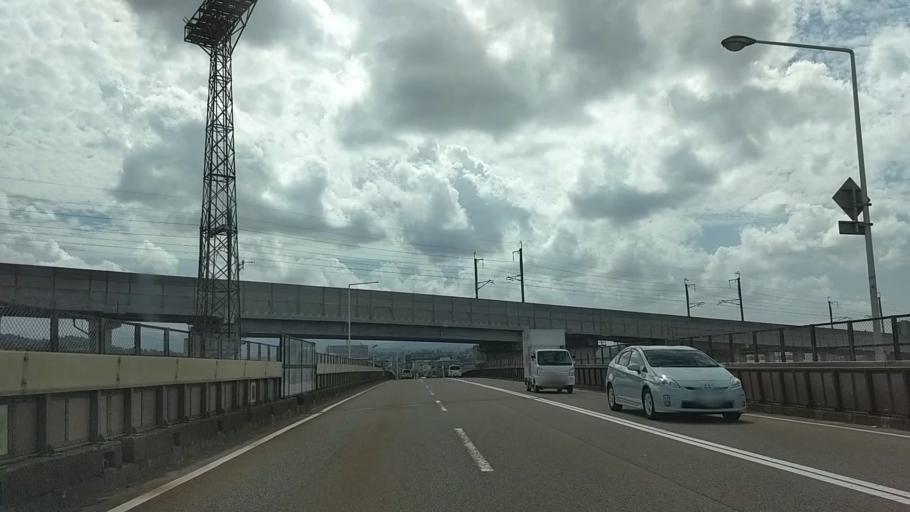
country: JP
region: Ishikawa
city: Kanazawa-shi
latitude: 36.5886
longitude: 136.6633
